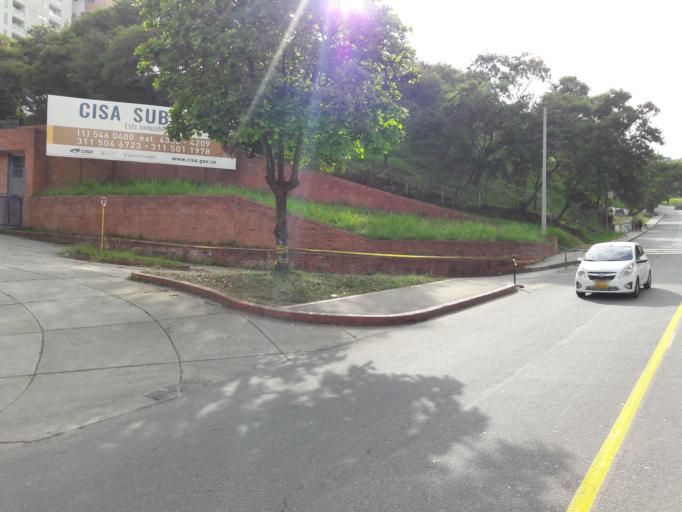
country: CO
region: Tolima
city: Ibague
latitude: 4.4364
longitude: -75.2051
